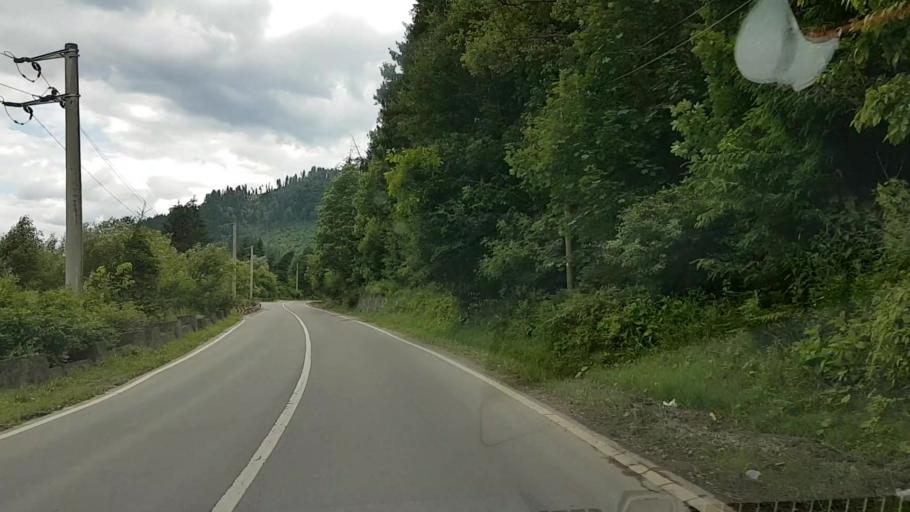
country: RO
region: Neamt
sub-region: Comuna Poiana Teiului
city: Poiana Teiului
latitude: 47.1024
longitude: 25.9401
